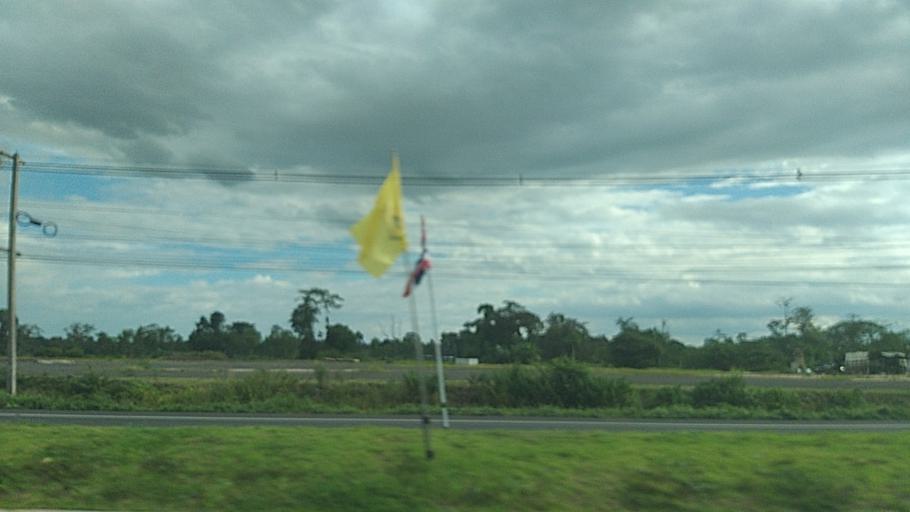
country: TH
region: Surin
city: Prasat
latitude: 14.6015
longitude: 103.4326
